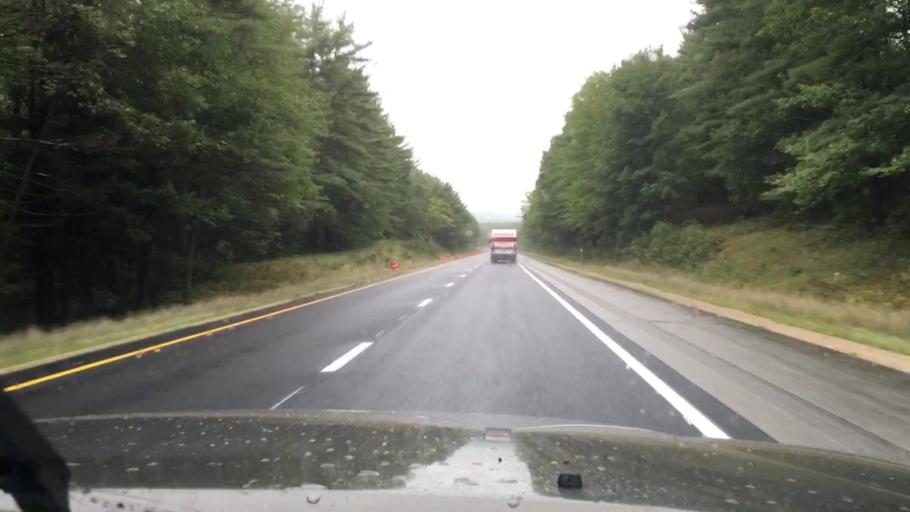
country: US
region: New Hampshire
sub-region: Merrimack County
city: Boscawen
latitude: 43.3690
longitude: -71.6111
